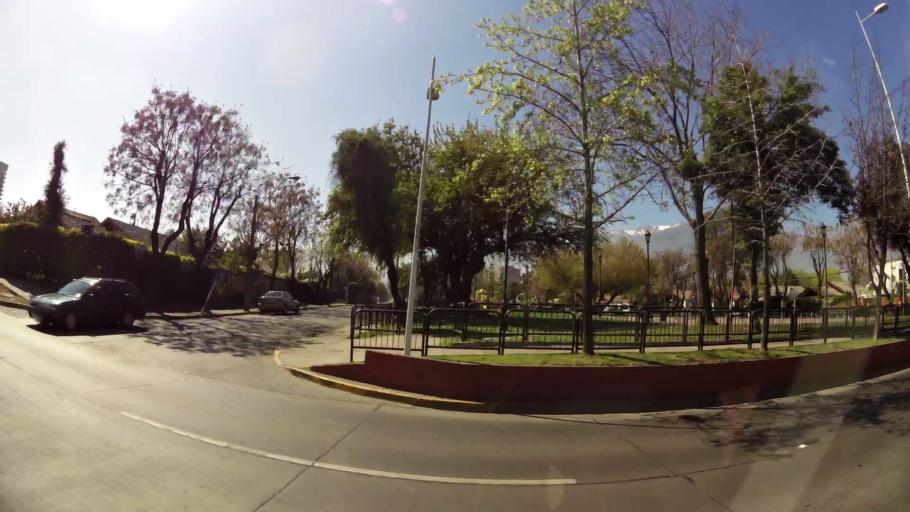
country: CL
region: Santiago Metropolitan
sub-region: Provincia de Santiago
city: Villa Presidente Frei, Nunoa, Santiago, Chile
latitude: -33.4289
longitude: -70.5542
